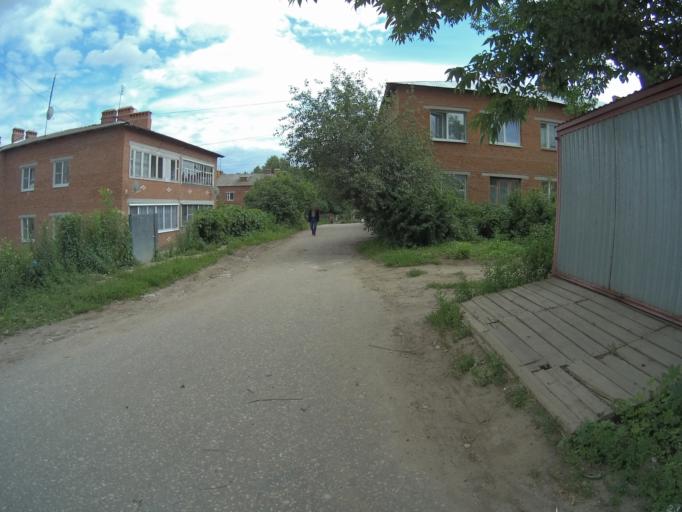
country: RU
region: Vladimir
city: Bogolyubovo
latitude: 56.1997
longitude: 40.5294
